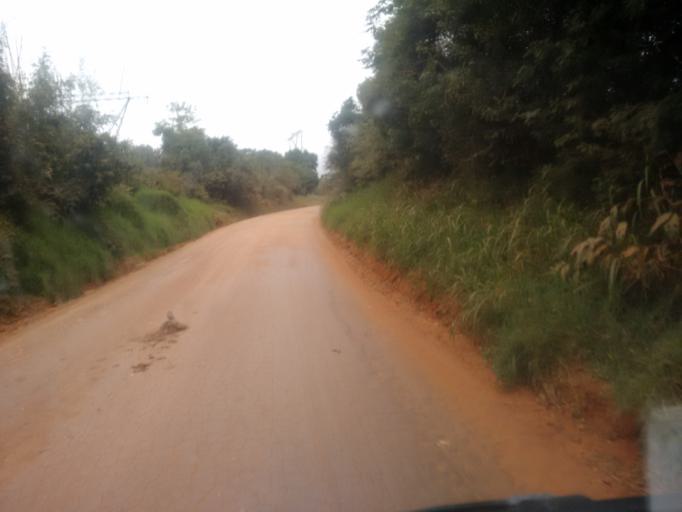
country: BR
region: Rio Grande do Sul
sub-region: Camaqua
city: Camaqua
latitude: -30.8264
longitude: -51.8153
